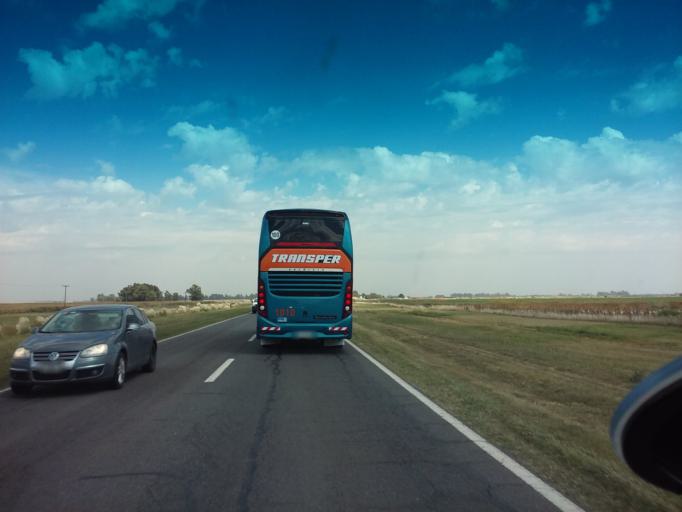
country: AR
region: Buenos Aires
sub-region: Partido de Carlos Casares
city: Carlos Casares
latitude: -35.6528
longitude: -61.3894
